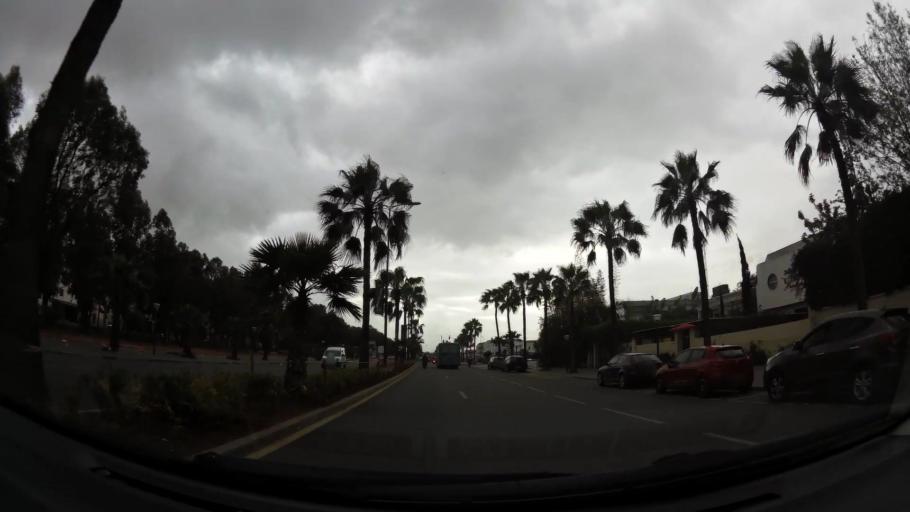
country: MA
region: Grand Casablanca
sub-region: Casablanca
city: Casablanca
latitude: 33.5738
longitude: -7.6841
